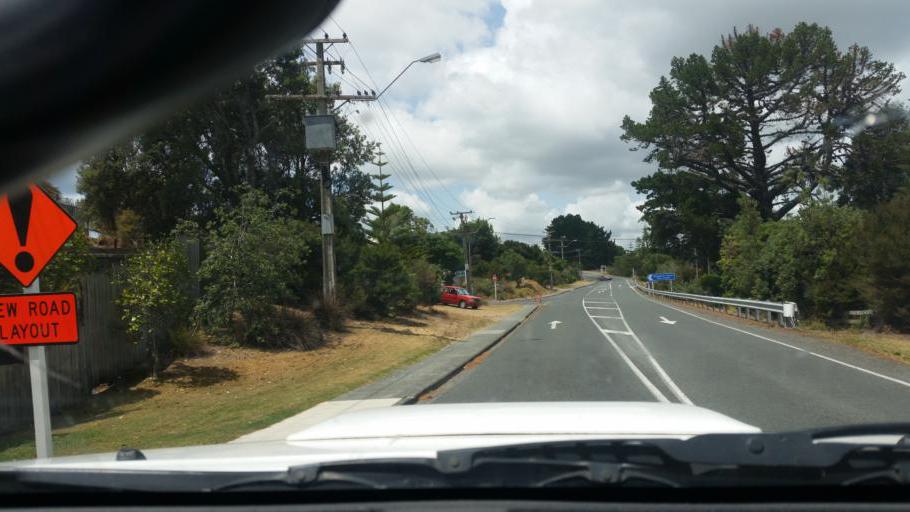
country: NZ
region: Auckland
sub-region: Auckland
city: Wellsford
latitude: -36.0948
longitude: 174.5859
